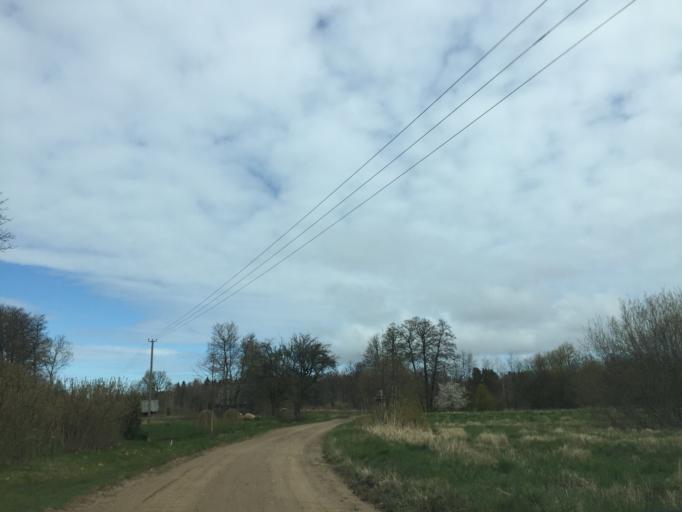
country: LV
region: Salacgrivas
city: Salacgriva
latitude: 57.5248
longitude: 24.3805
